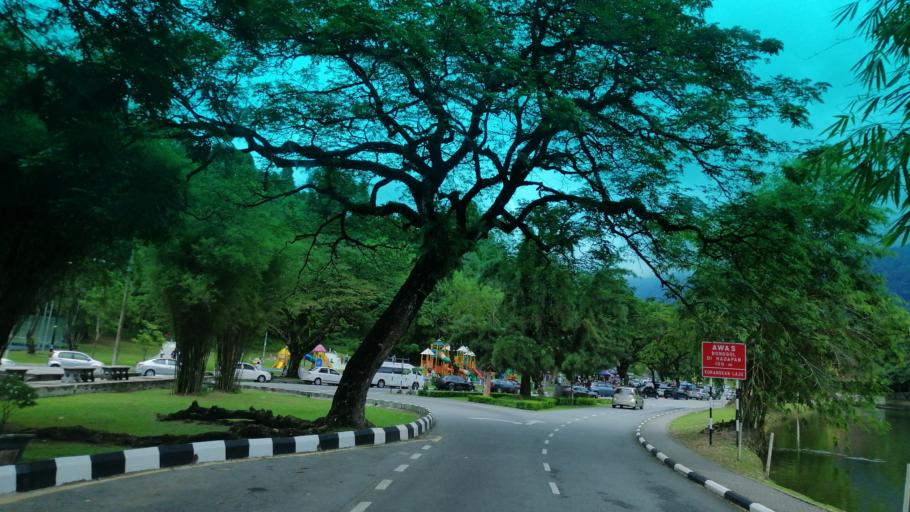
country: MY
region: Perak
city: Taiping
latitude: 4.8531
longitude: 100.7463
